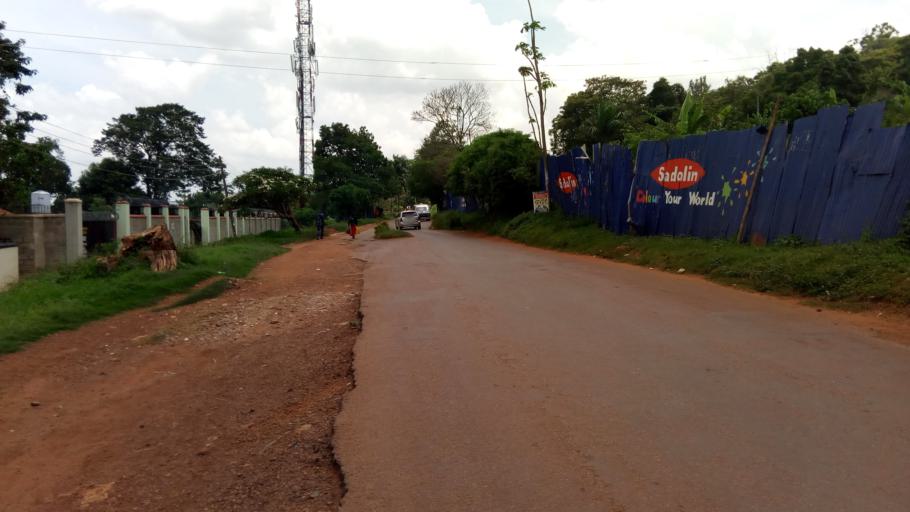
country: UG
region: Central Region
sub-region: Wakiso District
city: Kireka
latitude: 0.3229
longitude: 32.6315
